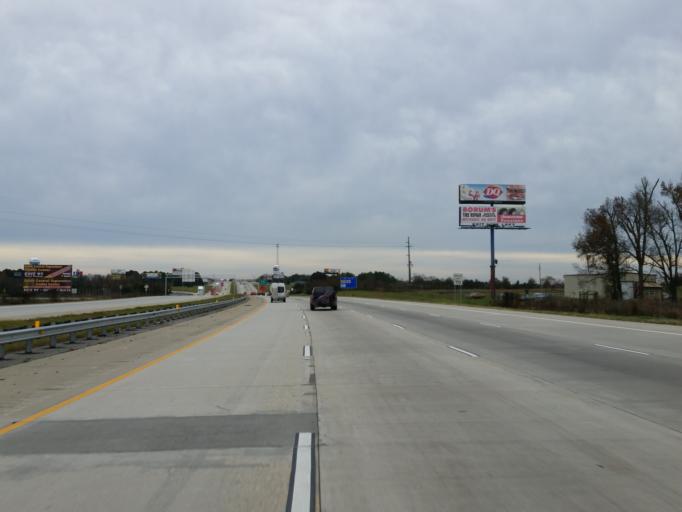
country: US
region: Georgia
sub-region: Dooly County
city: Unadilla
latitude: 32.2550
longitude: -83.7480
